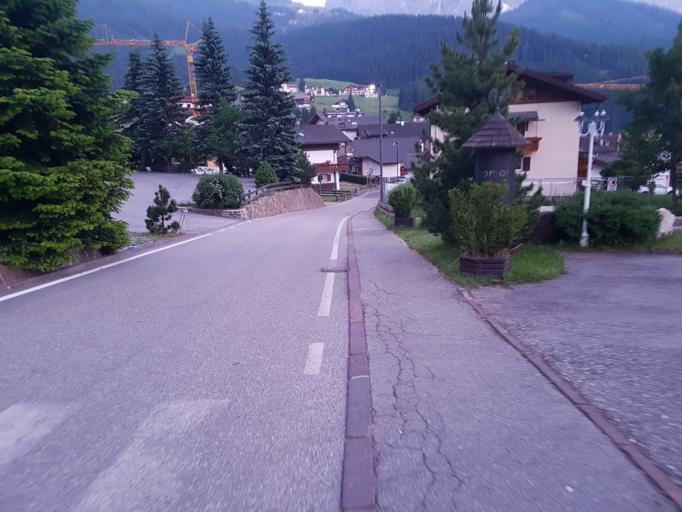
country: IT
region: Trentino-Alto Adige
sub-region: Bolzano
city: Santa Cristina Valgardena
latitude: 46.5624
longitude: 11.7355
